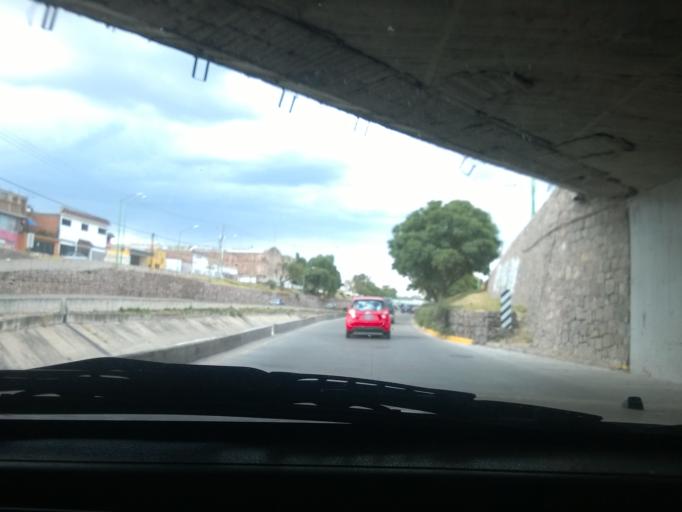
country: MX
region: Guanajuato
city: Leon
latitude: 21.1331
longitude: -101.6783
